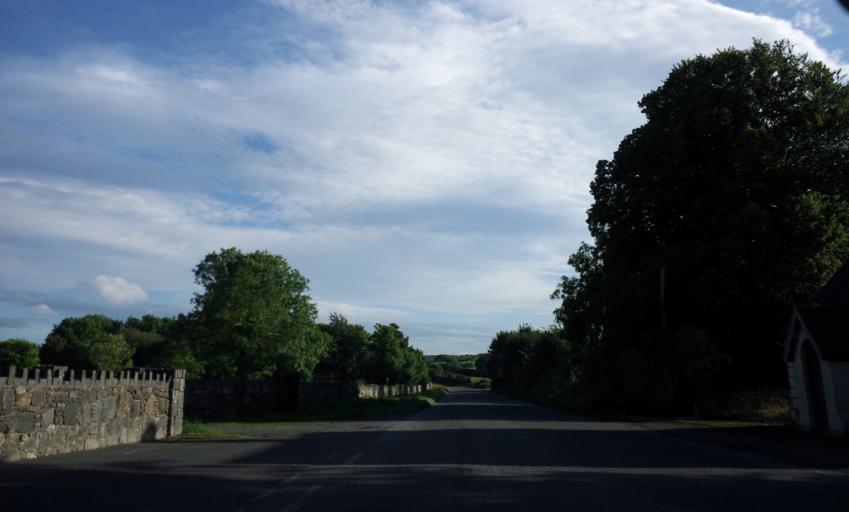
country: IE
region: Munster
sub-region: An Clar
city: Ennis
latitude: 52.8873
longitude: -9.0325
